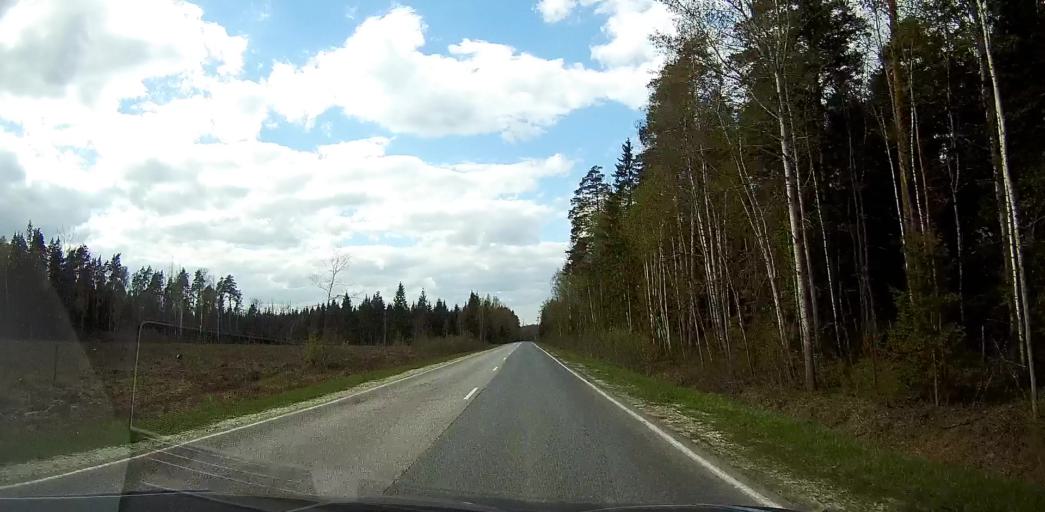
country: RU
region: Moskovskaya
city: Rakhmanovo
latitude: 55.6485
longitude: 38.6676
